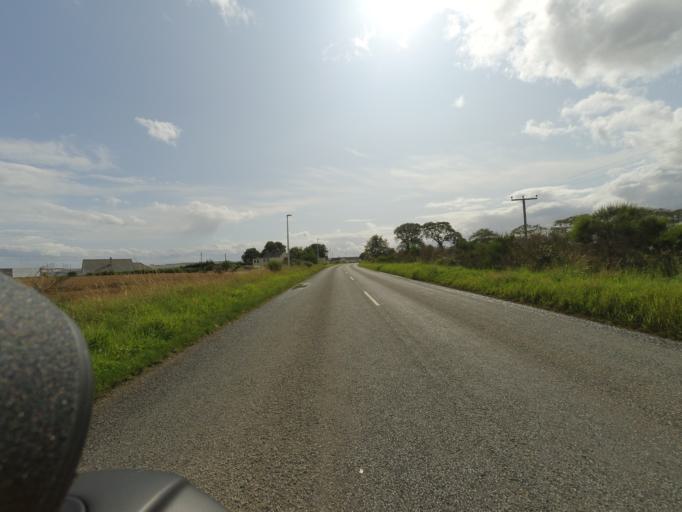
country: GB
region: Scotland
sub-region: Highland
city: Invergordon
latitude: 57.7262
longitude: -4.0965
